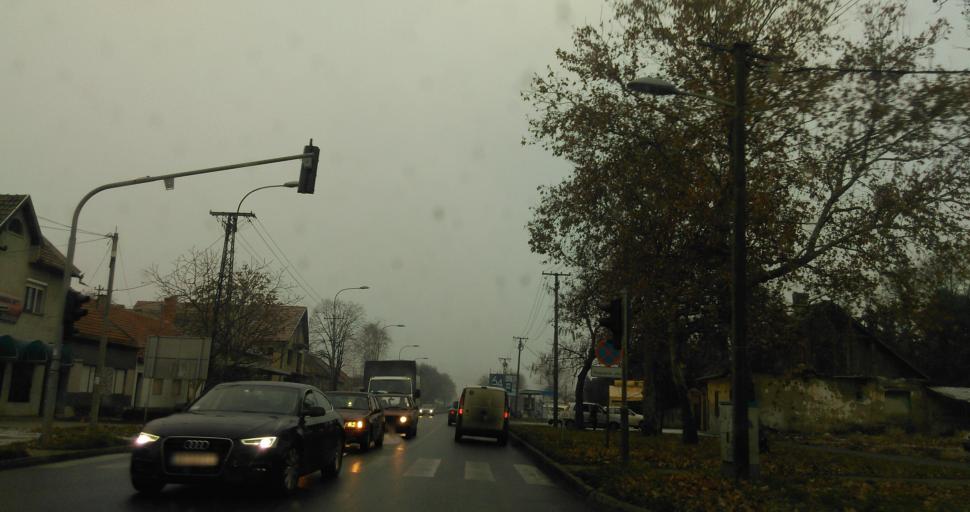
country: RS
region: Autonomna Pokrajina Vojvodina
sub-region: Srednjebanatski Okrug
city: Zrenjanin
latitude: 45.3767
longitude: 20.4084
